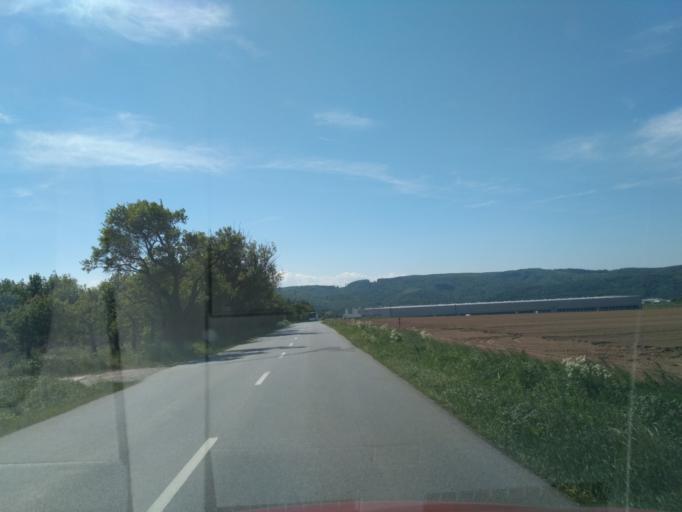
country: SK
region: Presovsky
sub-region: Okres Presov
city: Presov
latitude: 48.9504
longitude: 21.2722
